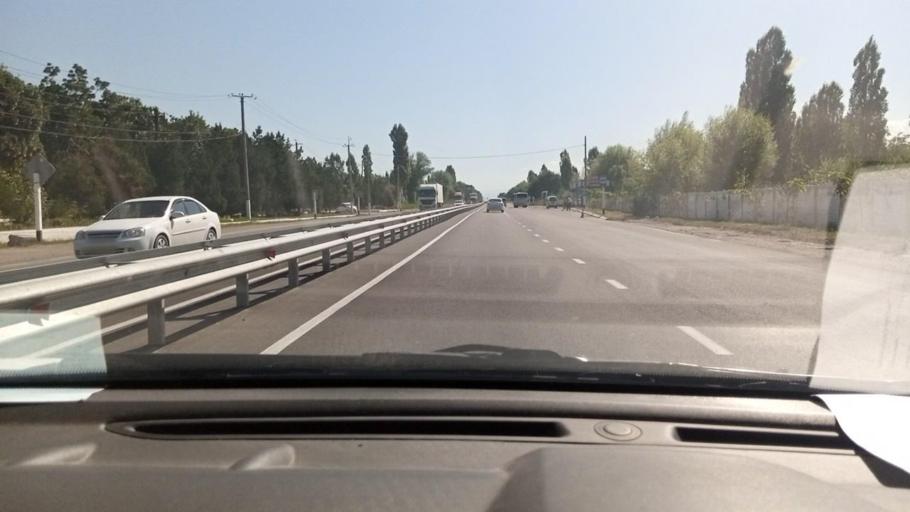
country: UZ
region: Toshkent
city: Angren
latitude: 40.9786
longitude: 70.0109
